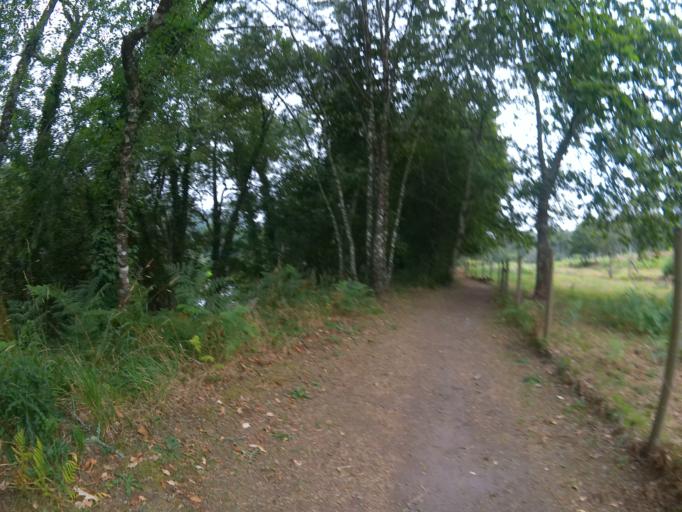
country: PT
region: Viana do Castelo
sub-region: Ponte da Barca
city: Ponte da Barca
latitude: 41.8069
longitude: -8.4324
